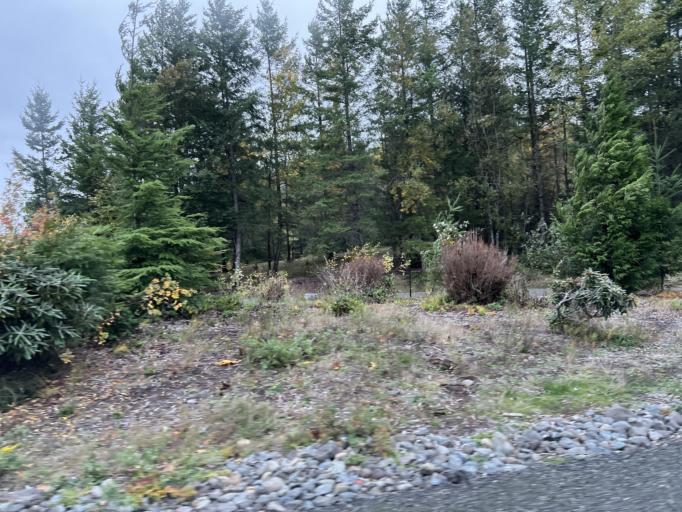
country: US
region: Washington
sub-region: King County
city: Snoqualmie
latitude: 47.5102
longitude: -121.8419
